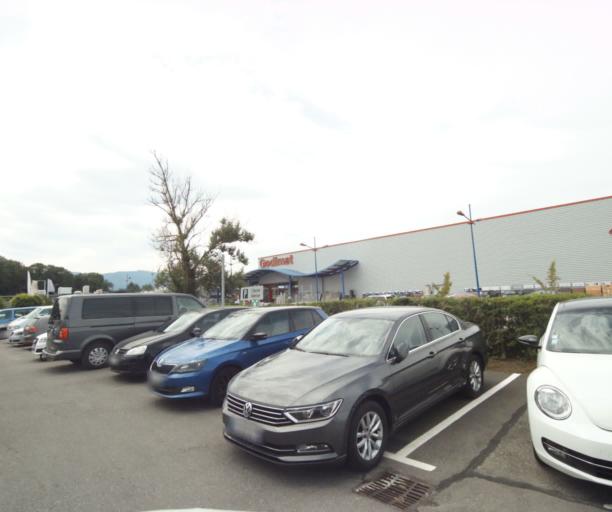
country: FR
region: Rhone-Alpes
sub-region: Departement de la Haute-Savoie
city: Anthy-sur-Leman
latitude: 46.3441
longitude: 6.4176
